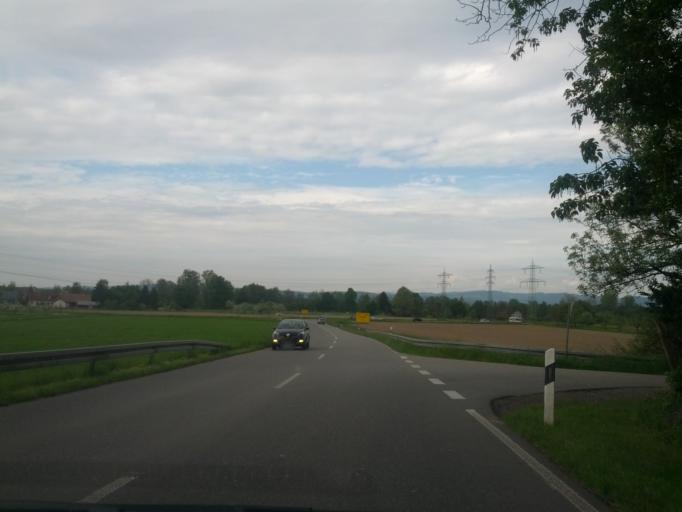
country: DE
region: Baden-Wuerttemberg
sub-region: Freiburg Region
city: Vorstetten
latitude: 48.0744
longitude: 7.8109
